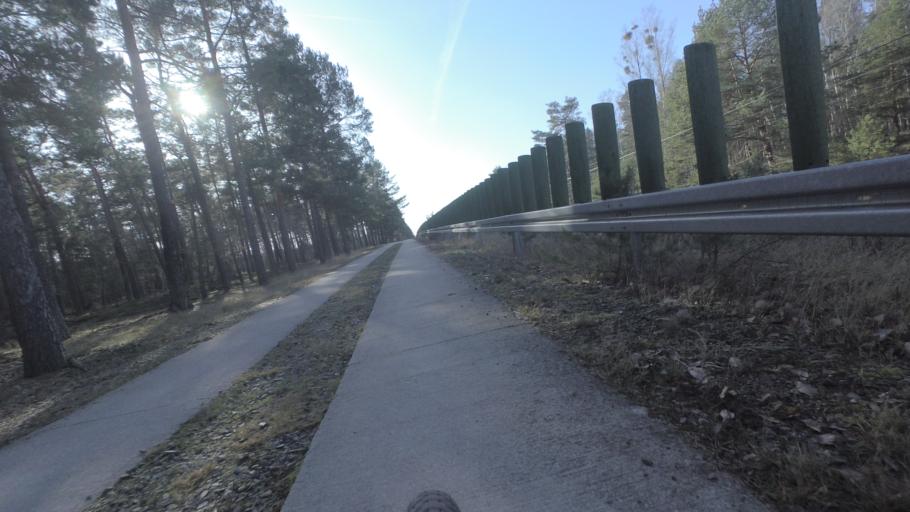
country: DE
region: Brandenburg
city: Trebbin
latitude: 52.1549
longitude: 13.2203
